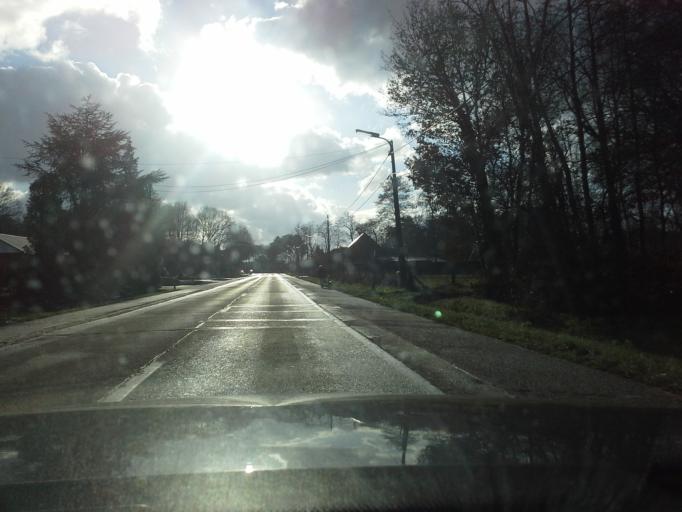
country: BE
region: Flanders
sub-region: Provincie Antwerpen
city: Mol
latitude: 51.1717
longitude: 5.1071
